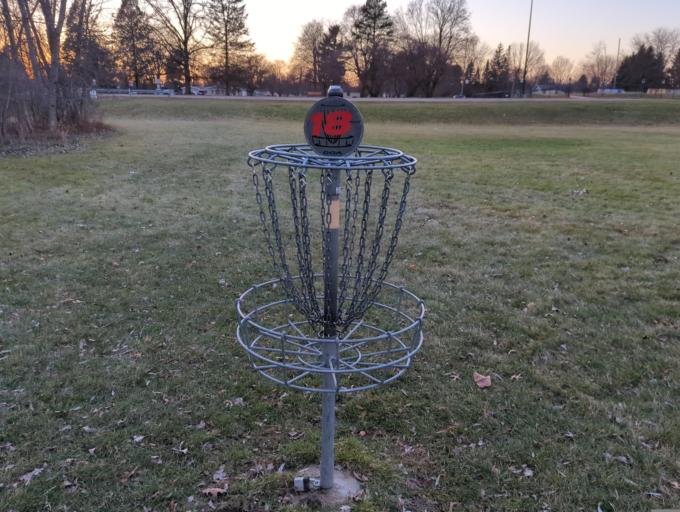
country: US
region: Michigan
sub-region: Eaton County
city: Charlotte
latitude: 42.5546
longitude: -84.8437
